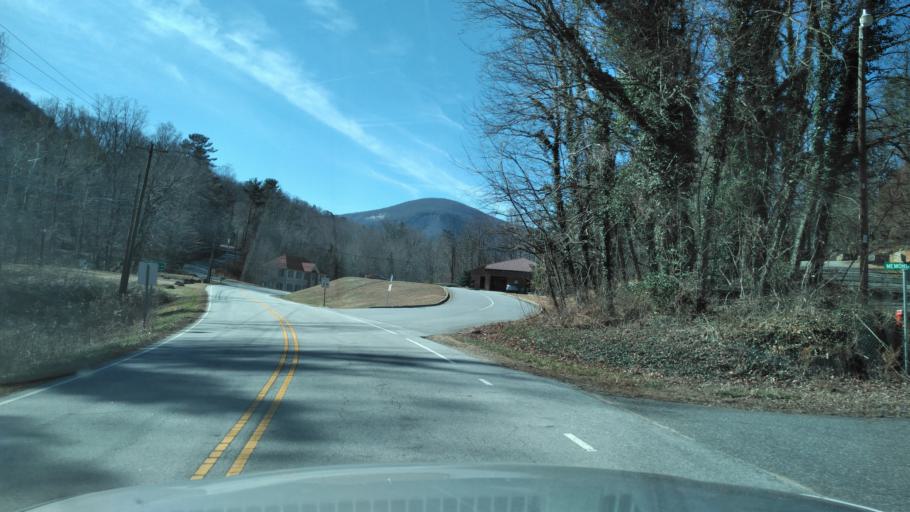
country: US
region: North Carolina
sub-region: Rutherford County
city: Lake Lure
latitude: 35.4314
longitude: -82.2195
